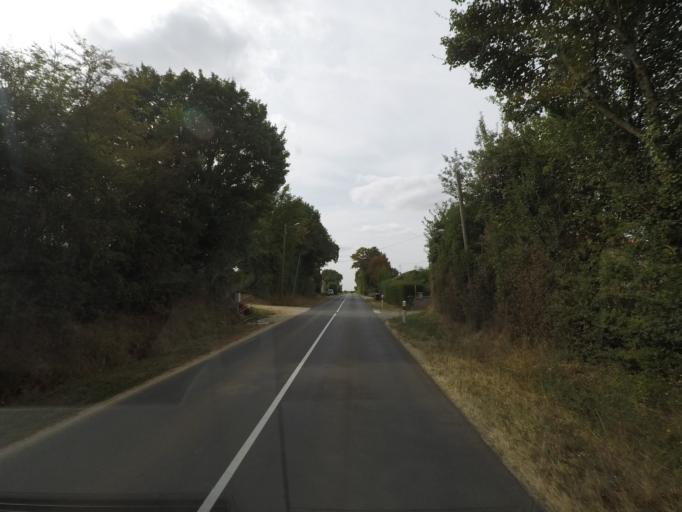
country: FR
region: Poitou-Charentes
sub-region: Departement de la Charente
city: Nanteuil-en-Vallee
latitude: 45.9871
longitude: 0.3426
